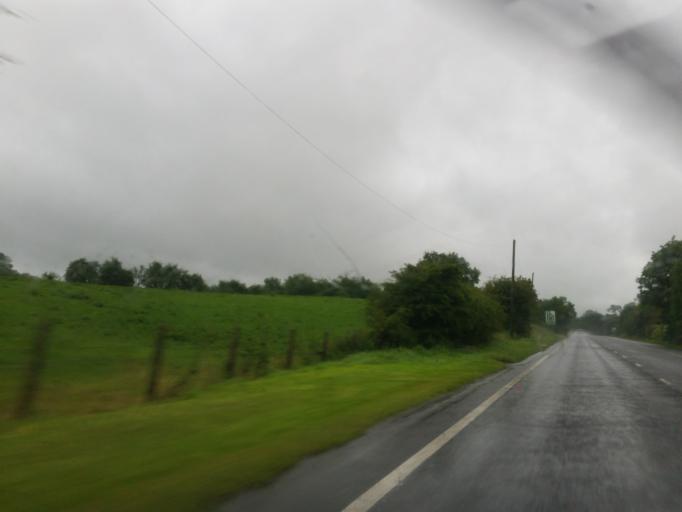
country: GB
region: Northern Ireland
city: Fivemiletown
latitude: 54.3818
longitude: -7.2772
